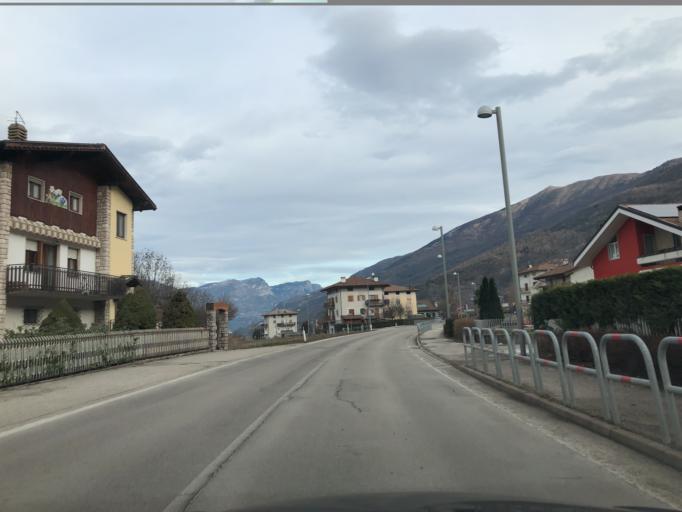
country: IT
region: Trentino-Alto Adige
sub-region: Provincia di Trento
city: Cavedine
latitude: 45.9762
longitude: 10.9752
